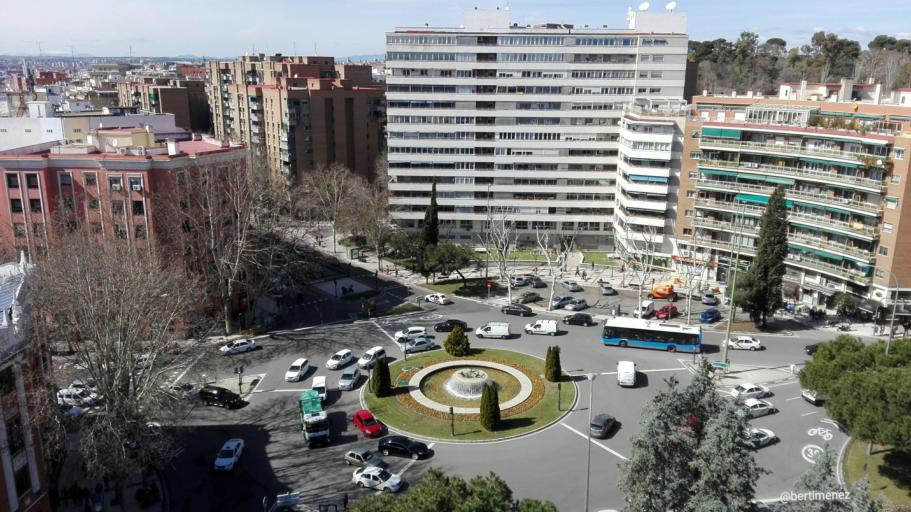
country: ES
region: Madrid
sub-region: Provincia de Madrid
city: Retiro
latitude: 40.4085
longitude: -3.6755
